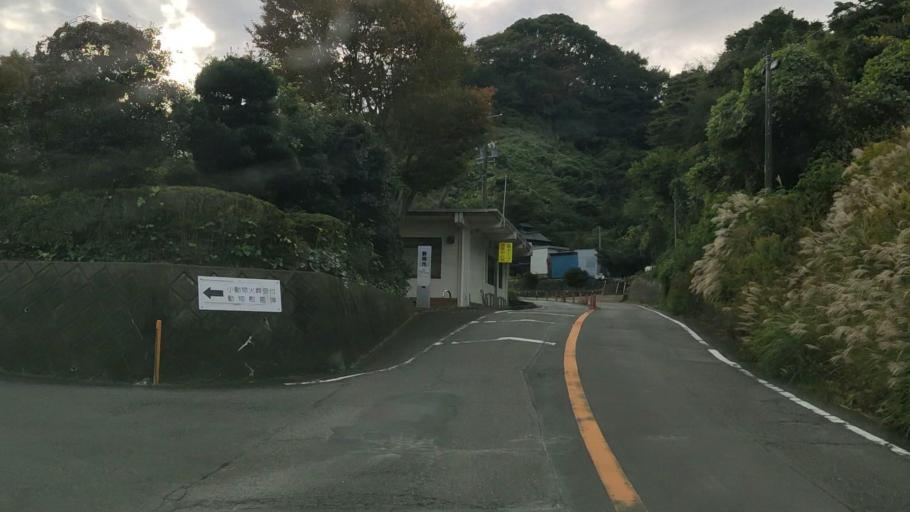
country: JP
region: Shizuoka
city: Shizuoka-shi
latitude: 34.9933
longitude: 138.4680
